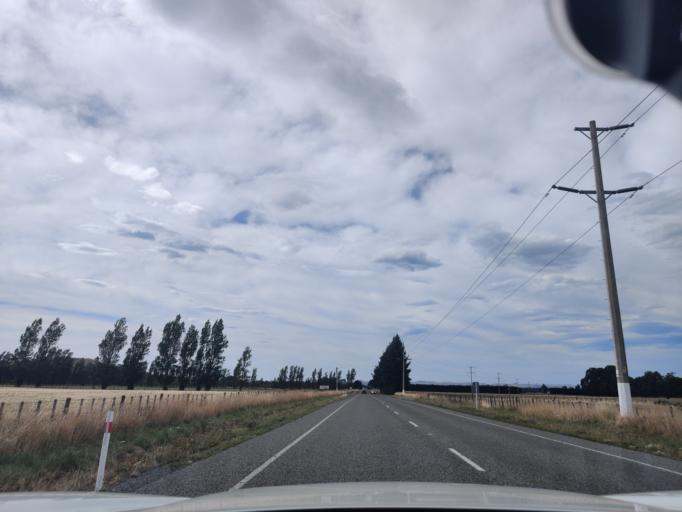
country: NZ
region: Wellington
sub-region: Masterton District
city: Masterton
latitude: -40.8515
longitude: 175.6365
